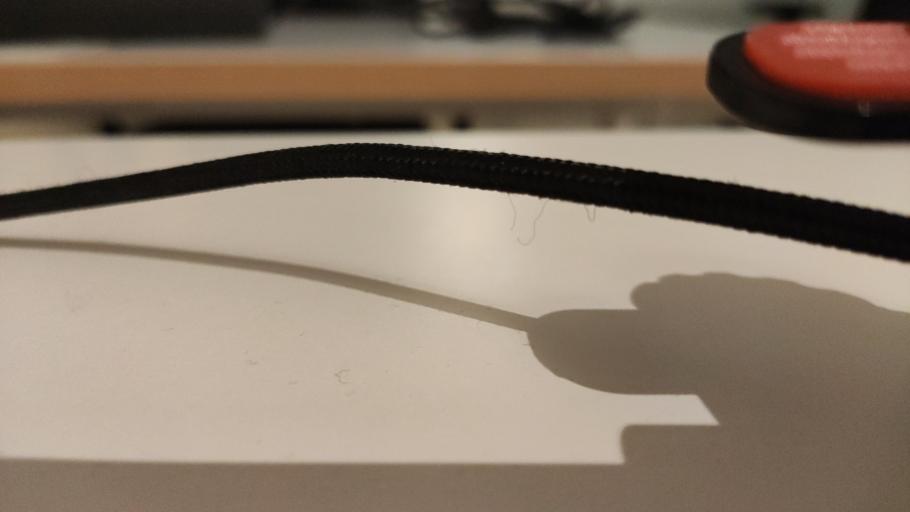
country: RU
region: Moskovskaya
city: Novoye
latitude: 55.6313
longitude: 38.9414
